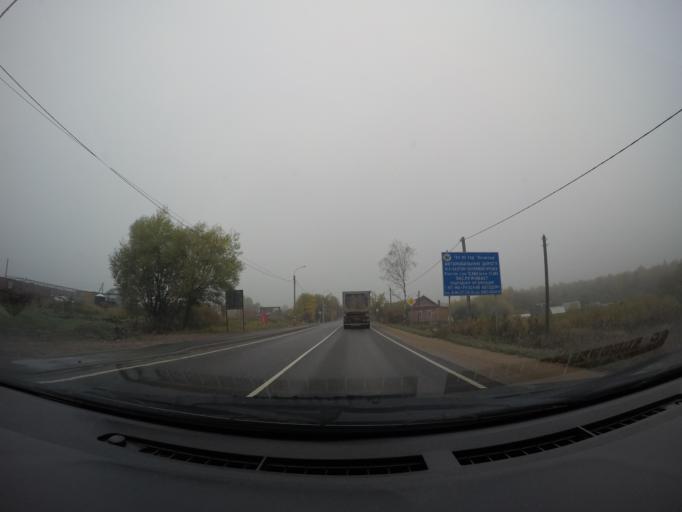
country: RU
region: Moskovskaya
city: Rumyantsevo
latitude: 55.8497
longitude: 36.5022
